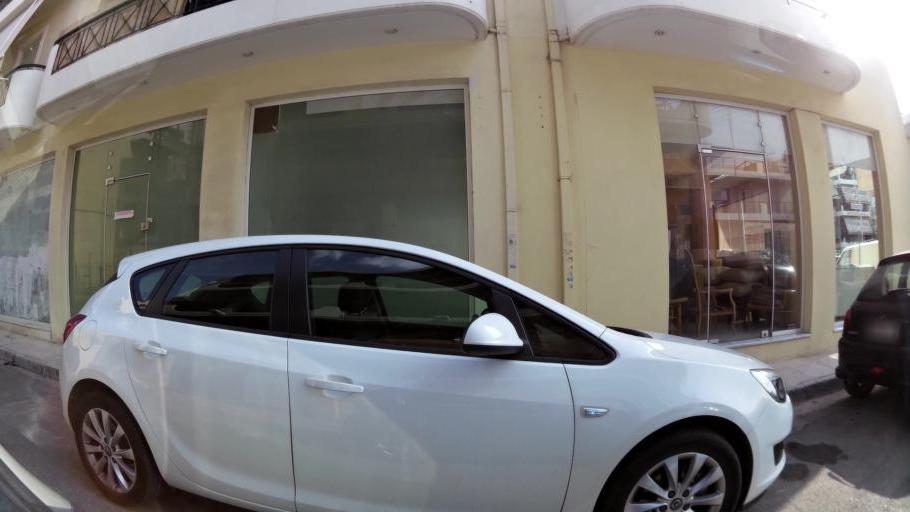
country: GR
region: Attica
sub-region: Nomarchia Athinas
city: Ilion
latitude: 38.0378
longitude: 23.7022
